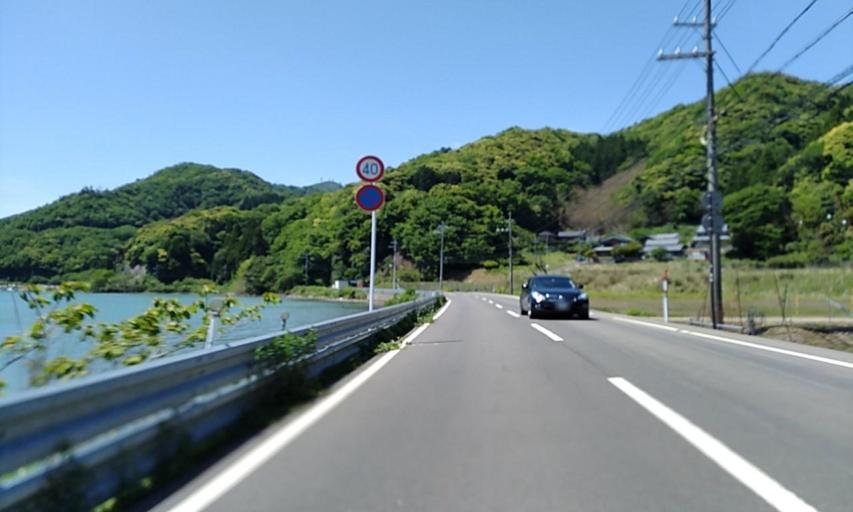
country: JP
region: Fukui
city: Obama
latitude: 35.5370
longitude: 135.7640
